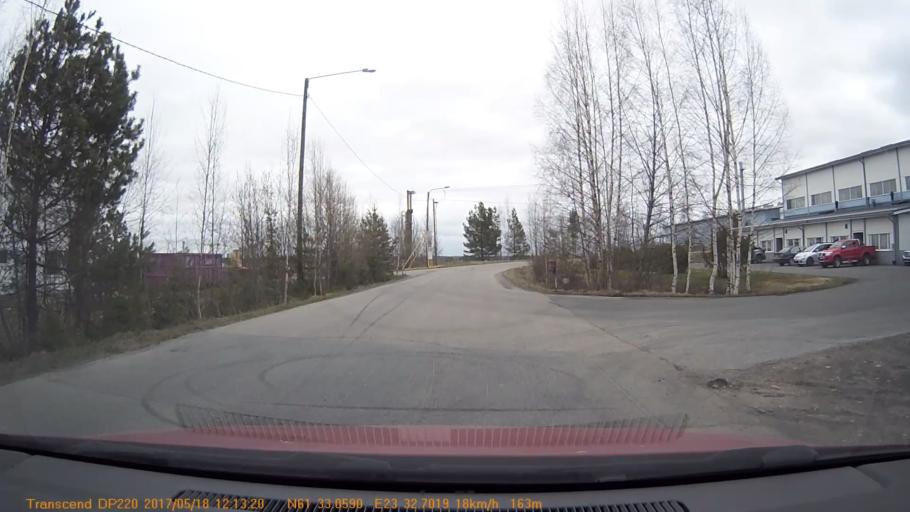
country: FI
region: Pirkanmaa
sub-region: Tampere
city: Yloejaervi
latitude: 61.5510
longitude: 23.5449
